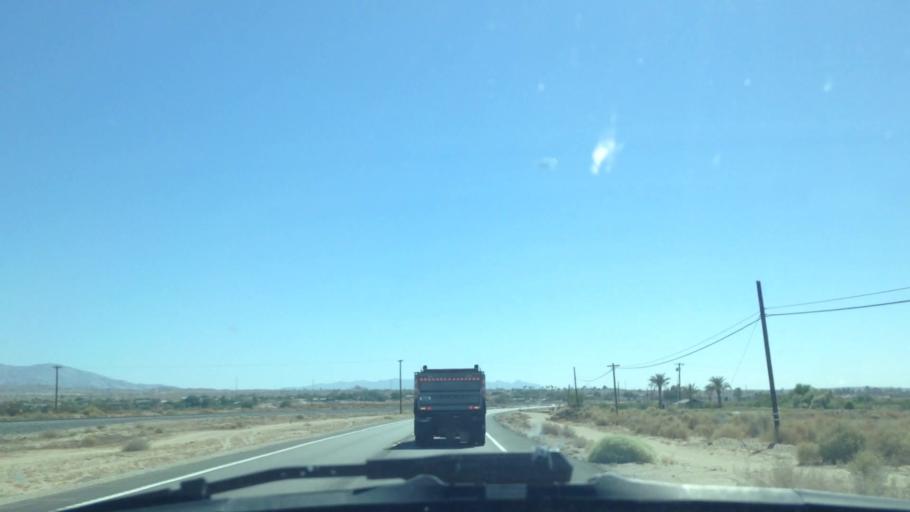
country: US
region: California
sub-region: Riverside County
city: Mecca
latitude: 33.5319
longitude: -115.9503
